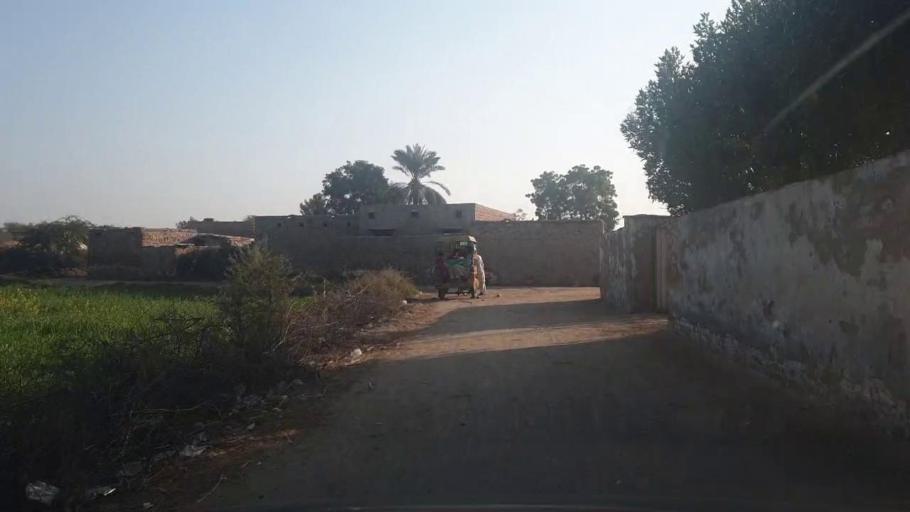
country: PK
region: Sindh
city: Sakrand
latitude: 26.0510
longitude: 68.3694
